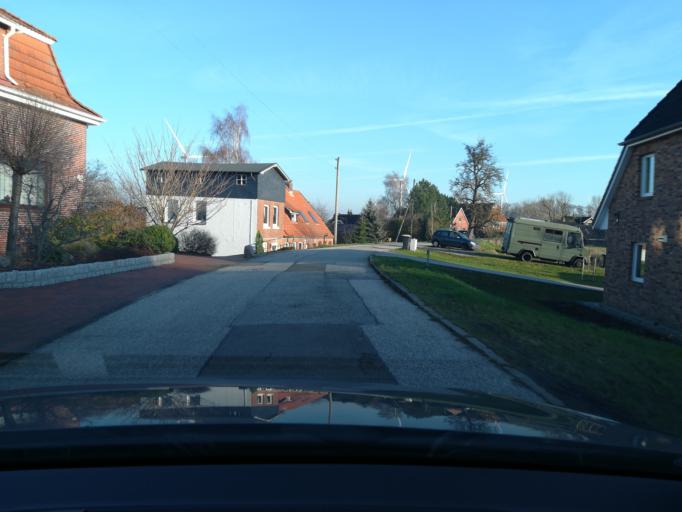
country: DE
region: Lower Saxony
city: Stelle
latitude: 53.4584
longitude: 10.0788
